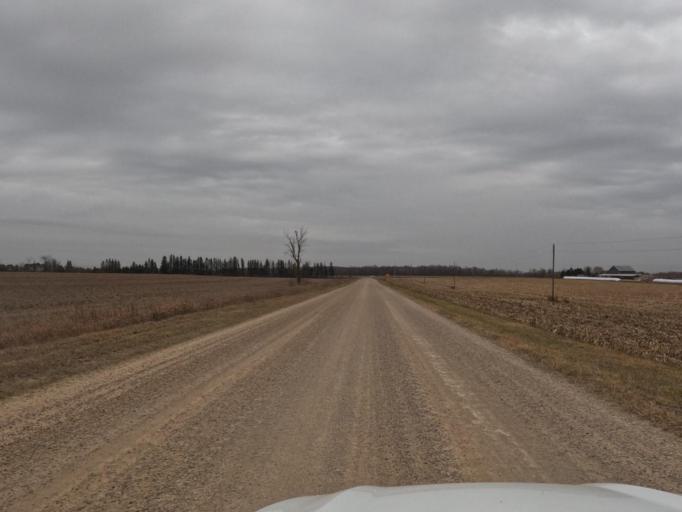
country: CA
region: Ontario
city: Shelburne
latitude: 43.8696
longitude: -80.3554
